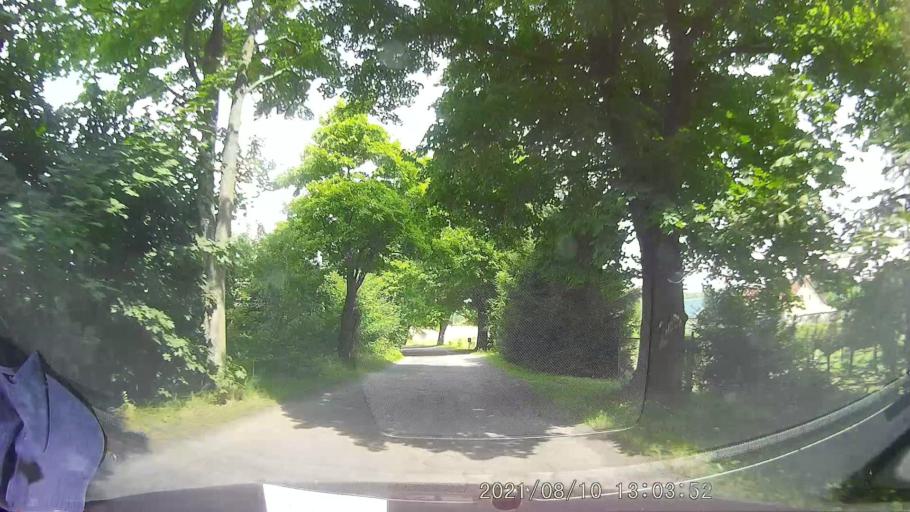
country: PL
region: Lower Silesian Voivodeship
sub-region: Powiat klodzki
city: Bozkow
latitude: 50.4734
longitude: 16.5637
